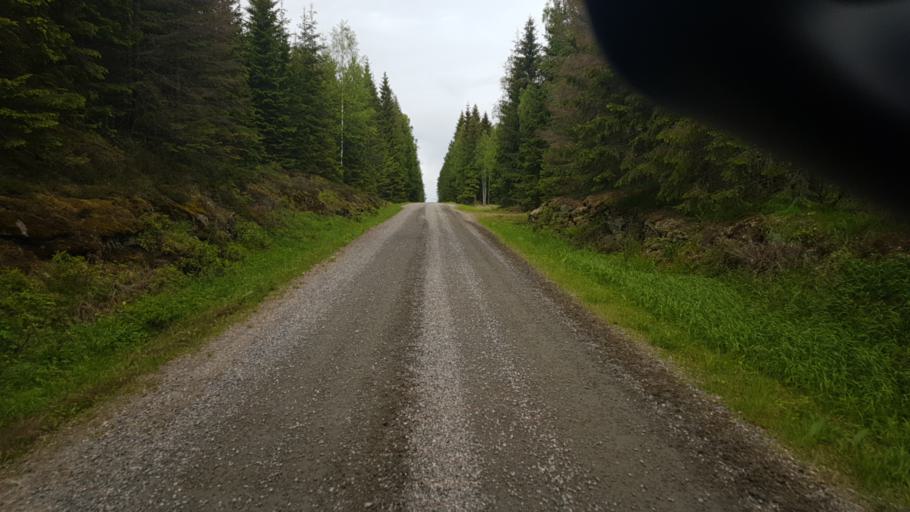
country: SE
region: Vaermland
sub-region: Eda Kommun
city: Charlottenberg
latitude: 60.0095
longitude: 12.5062
